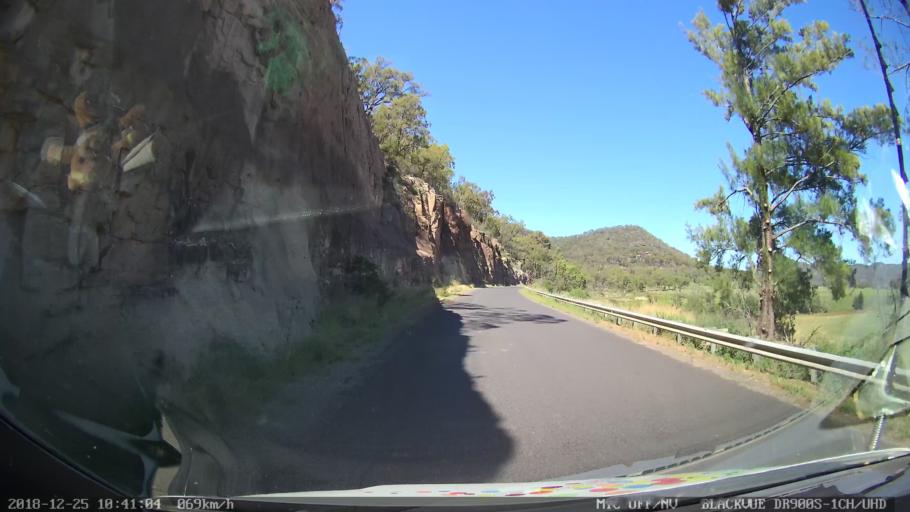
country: AU
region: New South Wales
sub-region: Upper Hunter Shire
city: Merriwa
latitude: -32.4140
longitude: 150.3387
